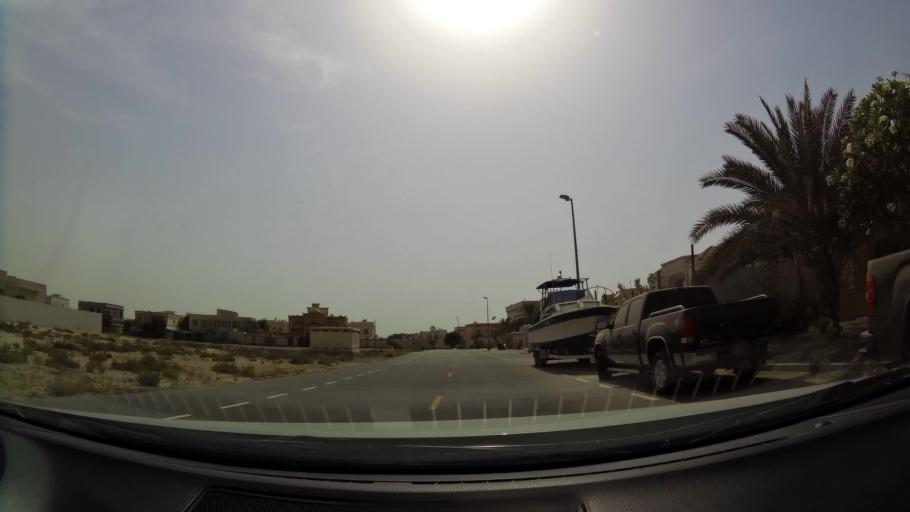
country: AE
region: Ash Shariqah
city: Sharjah
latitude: 25.2555
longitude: 55.4365
